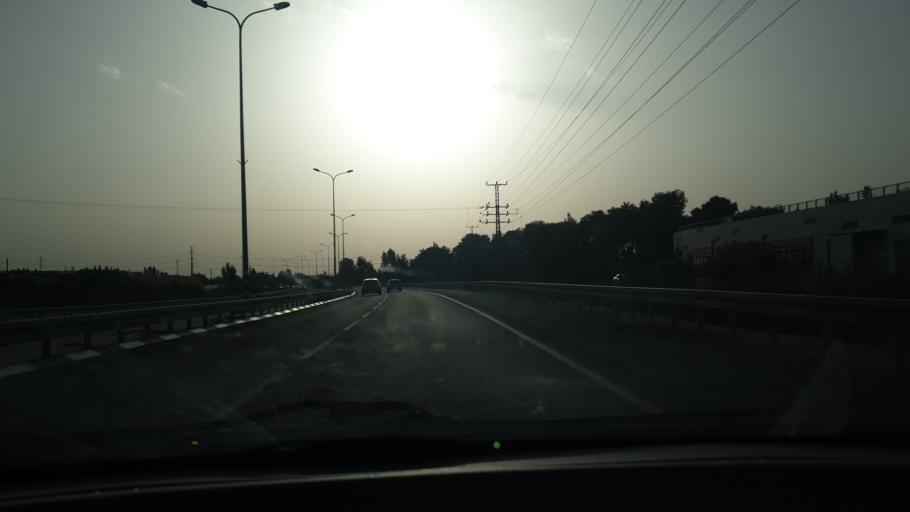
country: IL
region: Central District
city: Tel Mond
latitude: 32.2597
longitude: 34.9047
